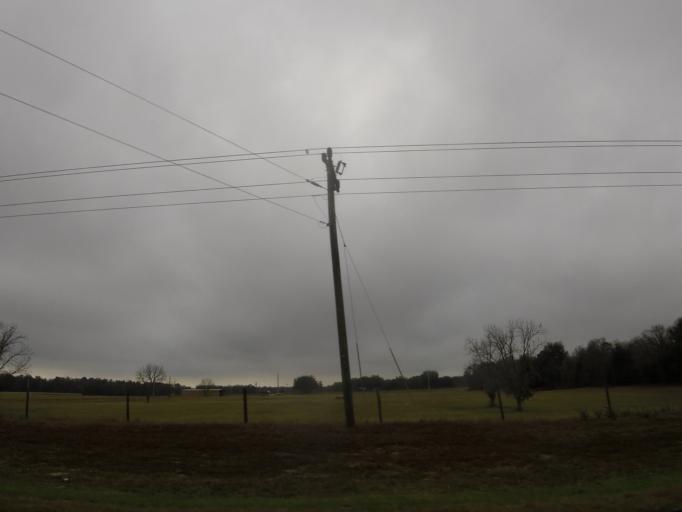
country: US
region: Florida
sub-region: Gilchrist County
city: Trenton
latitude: 29.7962
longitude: -82.8444
